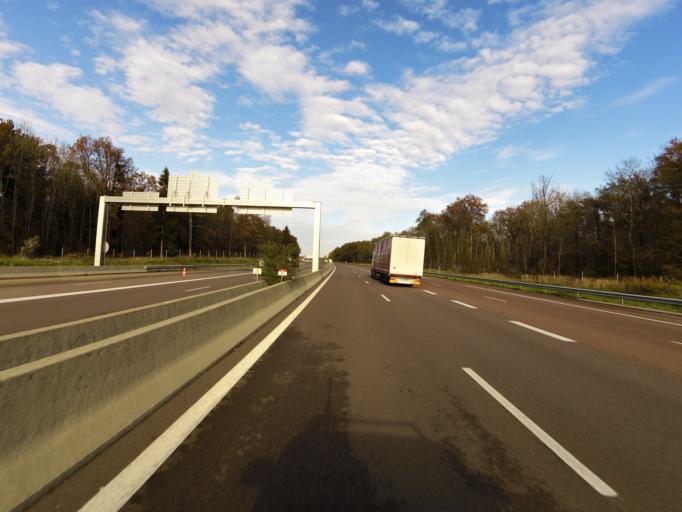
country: FR
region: Bourgogne
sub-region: Departement de la Cote-d'Or
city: Chevigny-Saint-Sauveur
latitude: 47.2773
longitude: 5.1491
